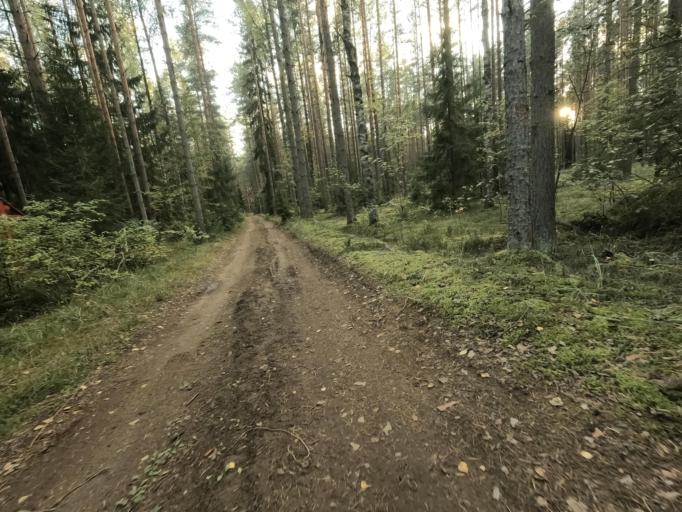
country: RU
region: Leningrad
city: Otradnoye
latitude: 59.8336
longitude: 30.7635
